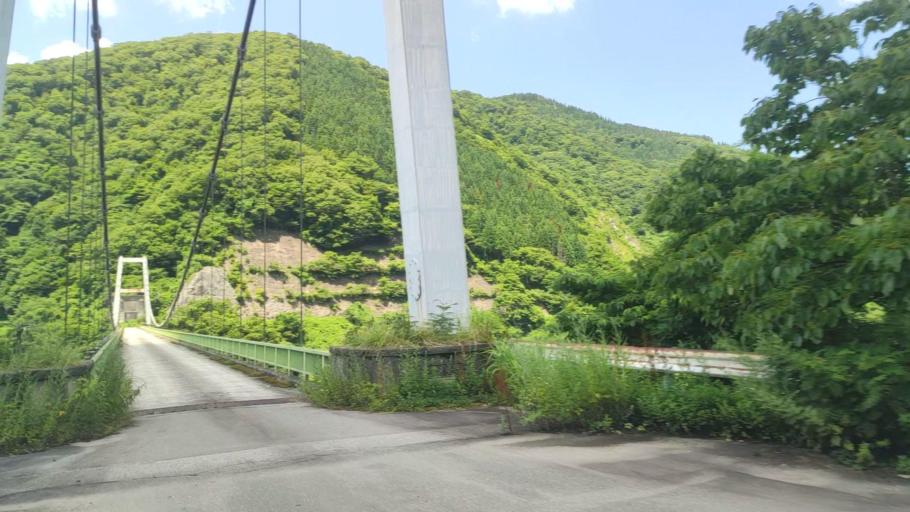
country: JP
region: Fukui
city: Ono
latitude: 35.8951
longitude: 136.5272
